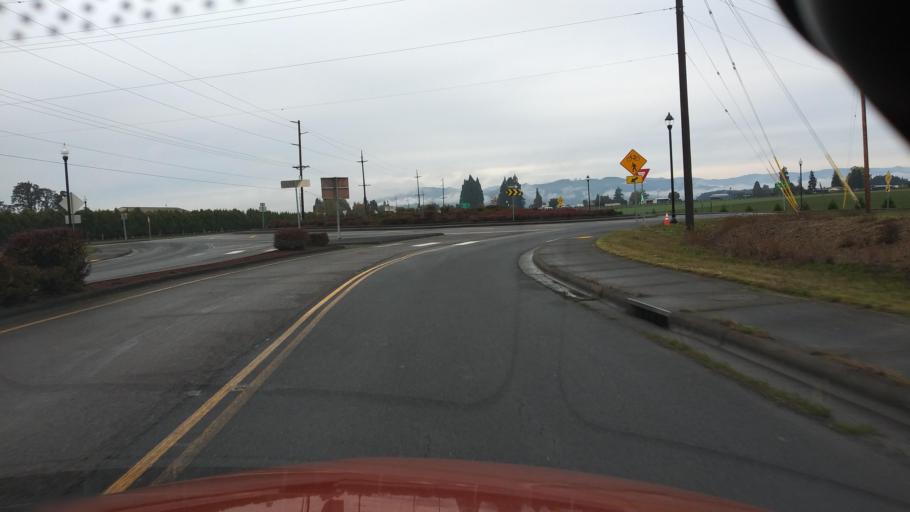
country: US
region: Oregon
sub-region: Washington County
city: Cornelius
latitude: 45.5516
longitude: -123.0724
